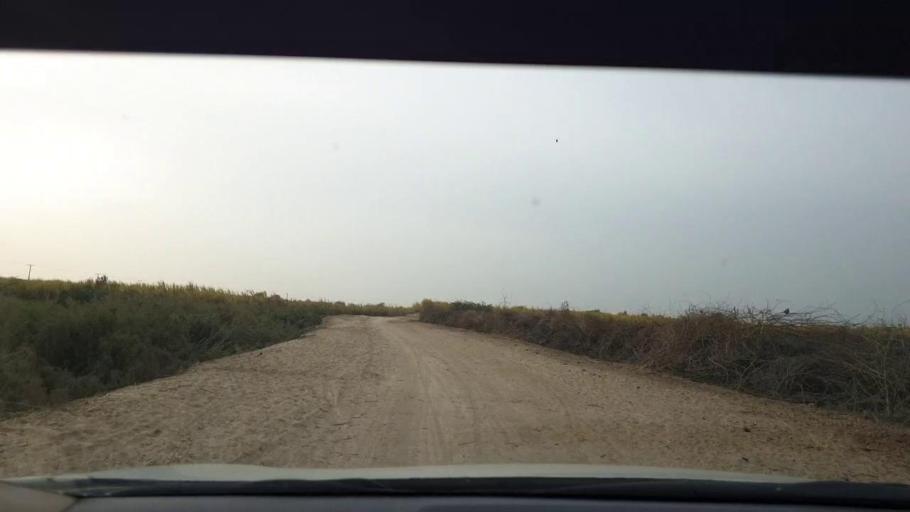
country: PK
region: Sindh
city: Jhol
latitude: 25.9057
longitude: 68.7910
